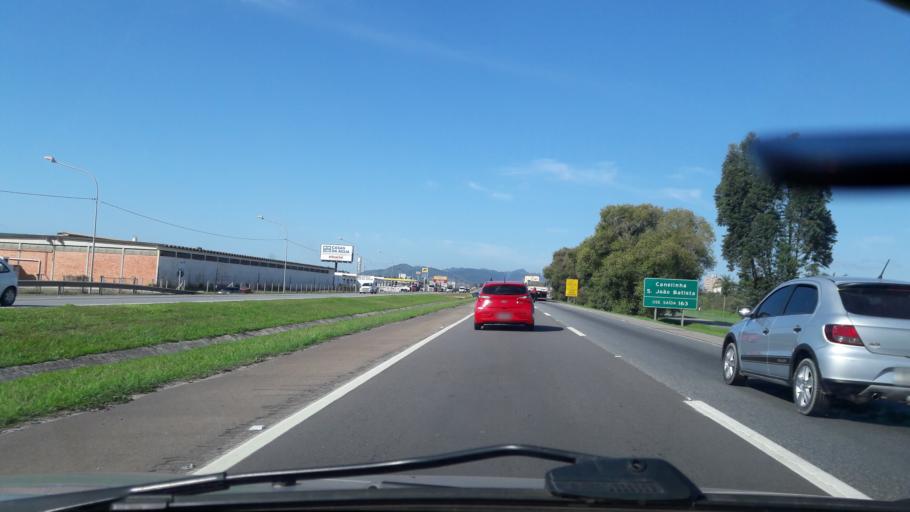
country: BR
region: Santa Catarina
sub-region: Tijucas
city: Tijucas
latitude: -27.2259
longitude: -48.6280
